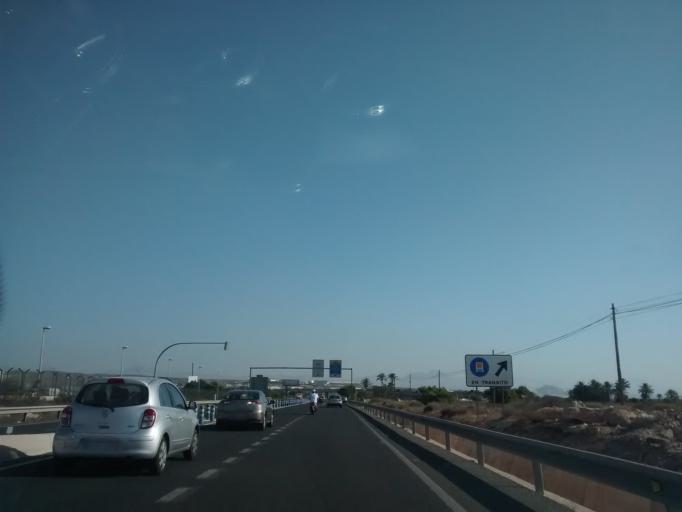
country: ES
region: Valencia
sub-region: Provincia de Alicante
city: Alicante
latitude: 38.2796
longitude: -0.5370
